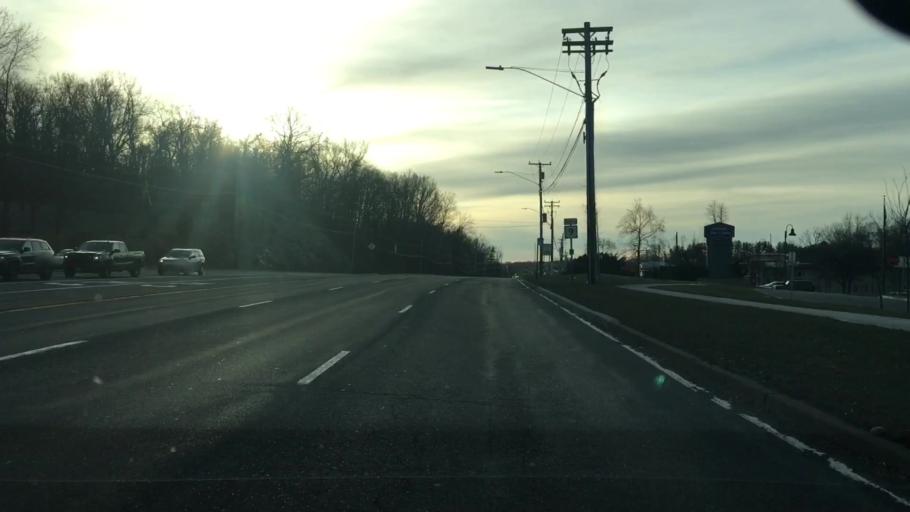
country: US
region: New York
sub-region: Dutchess County
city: Spackenkill
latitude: 41.6511
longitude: -73.9283
